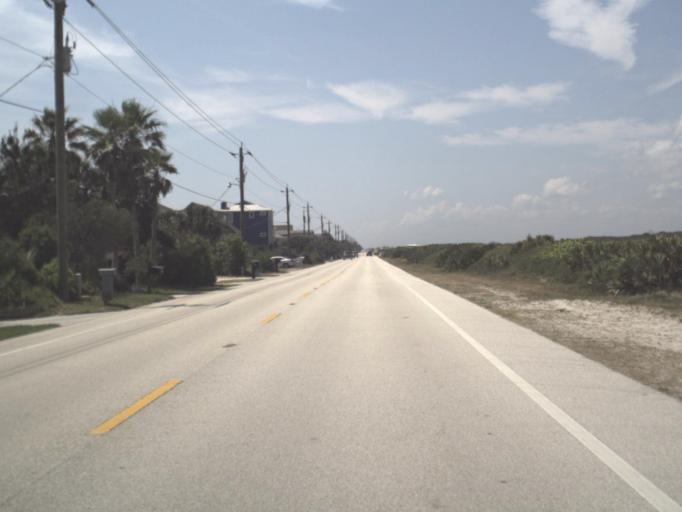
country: US
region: Florida
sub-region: Saint Johns County
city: Villano Beach
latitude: 30.0110
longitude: -81.3204
